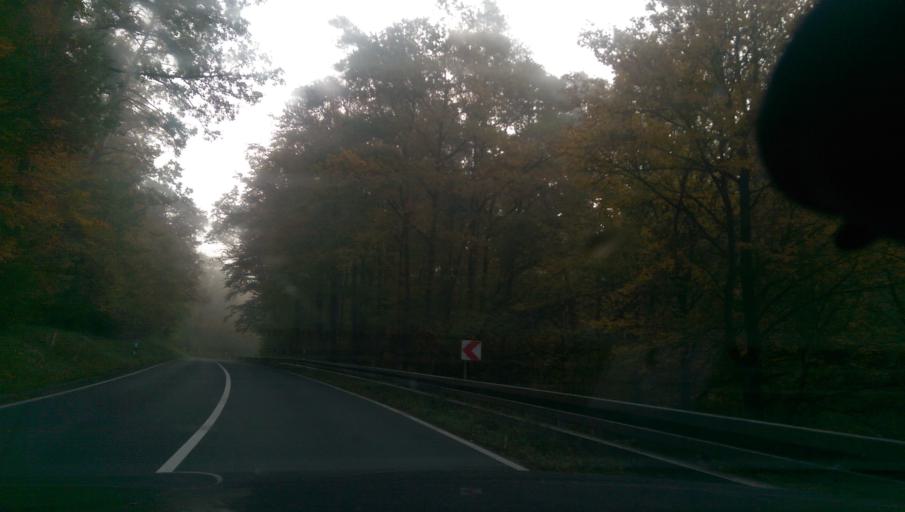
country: DE
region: Bavaria
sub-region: Regierungsbezirk Unterfranken
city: Oerlenbach
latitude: 50.1548
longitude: 10.1030
